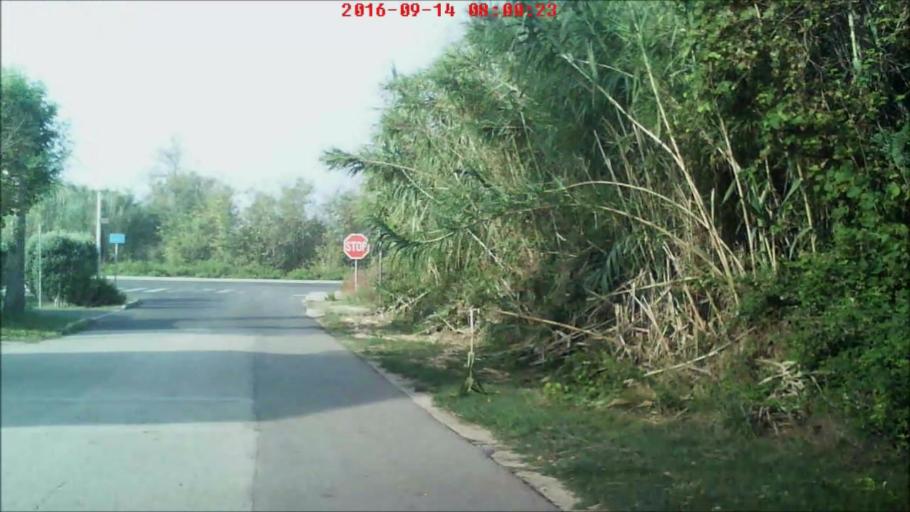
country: HR
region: Zadarska
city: Nin
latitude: 44.2567
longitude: 15.1561
